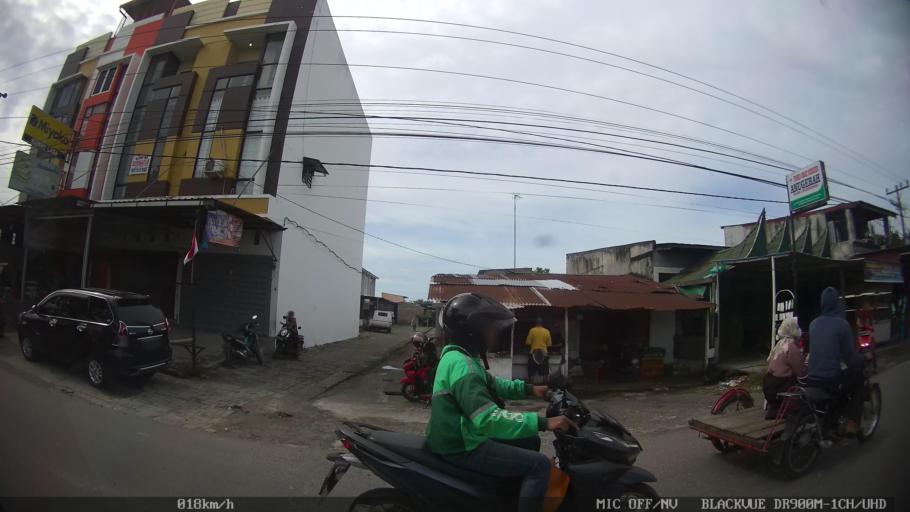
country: ID
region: North Sumatra
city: Medan
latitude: 3.6210
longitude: 98.7225
